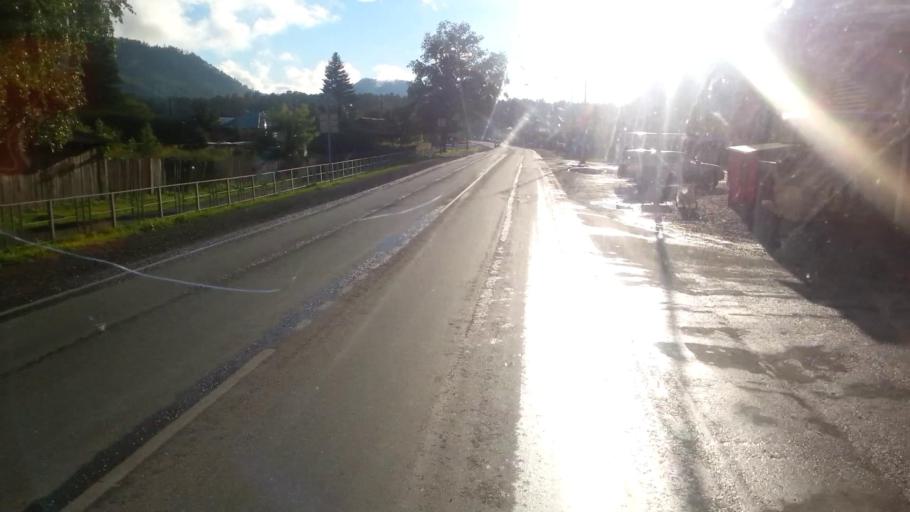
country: RU
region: Altay
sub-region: Mayminskiy Rayon
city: Manzherok
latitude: 51.8338
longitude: 85.7755
